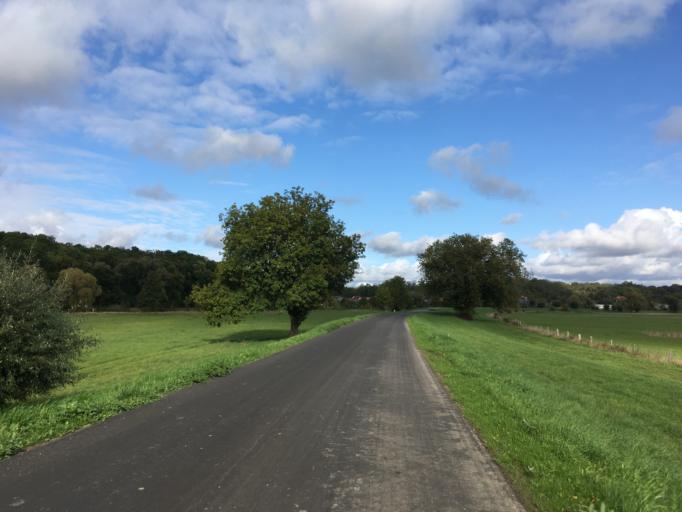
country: DE
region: Brandenburg
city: Schoneberg
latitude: 52.9722
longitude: 14.1123
